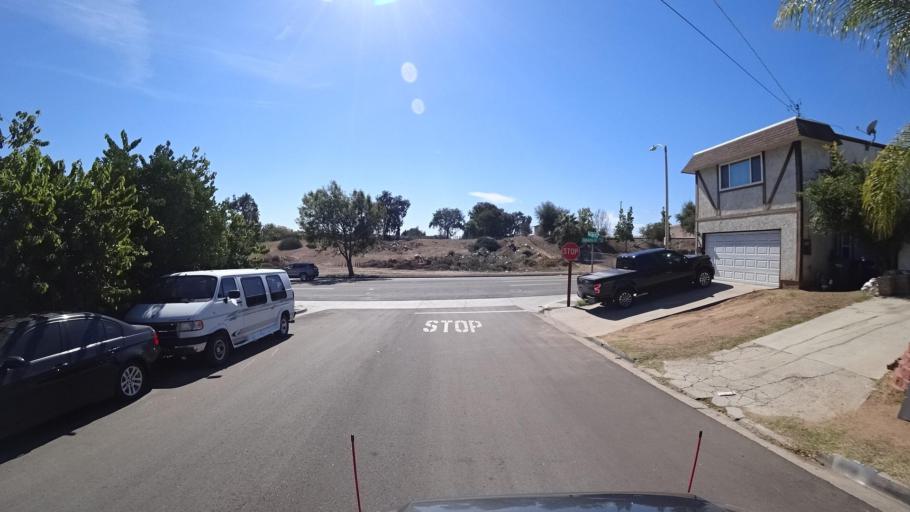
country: US
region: California
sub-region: San Diego County
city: La Presa
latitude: 32.7082
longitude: -116.9908
